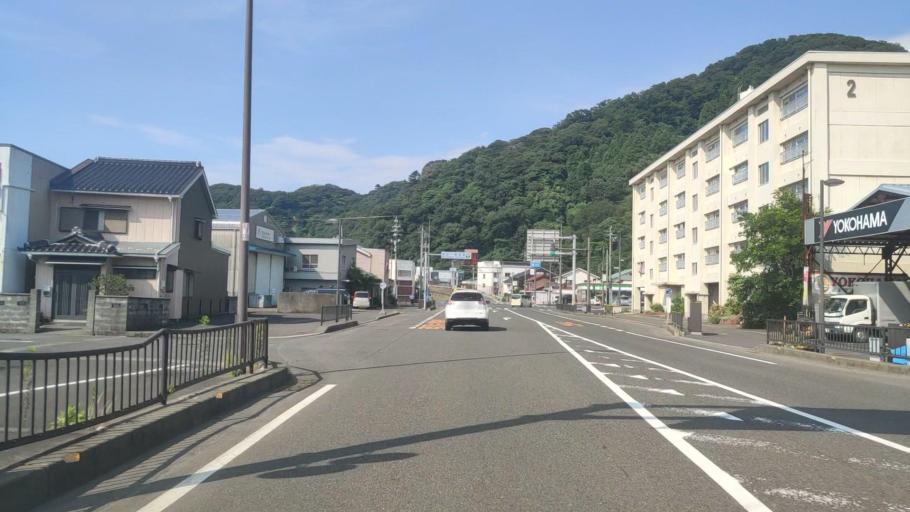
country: JP
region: Fukui
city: Tsuruga
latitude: 35.6576
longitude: 136.0757
